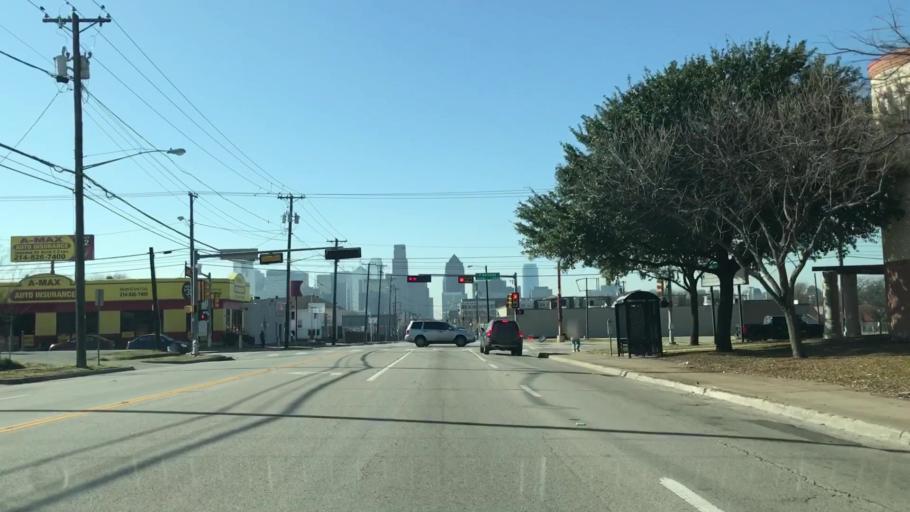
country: US
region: Texas
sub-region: Dallas County
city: Highland Park
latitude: 32.8031
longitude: -96.7800
